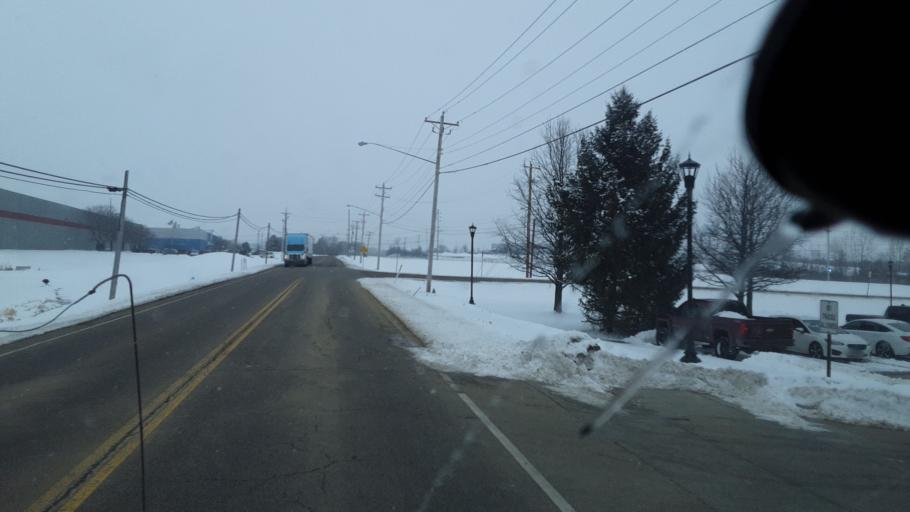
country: US
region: Ohio
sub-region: Licking County
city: Hebron
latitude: 39.9688
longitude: -82.4896
